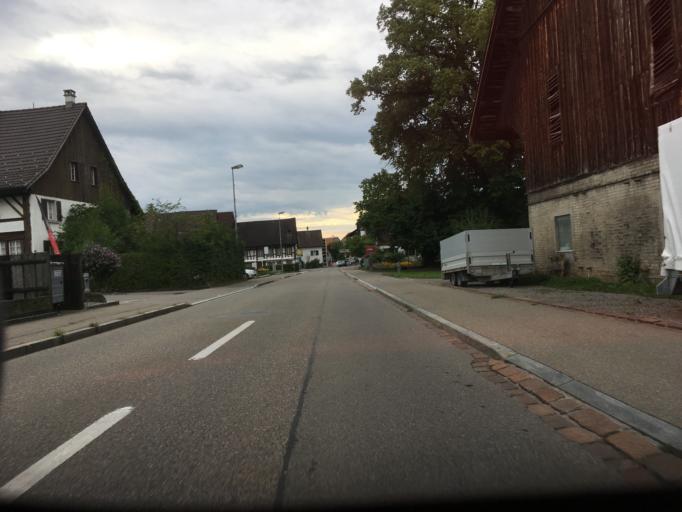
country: CH
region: Zurich
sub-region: Bezirk Uster
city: Volketswil / Volketswil (Dorf)
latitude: 47.3890
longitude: 8.6958
